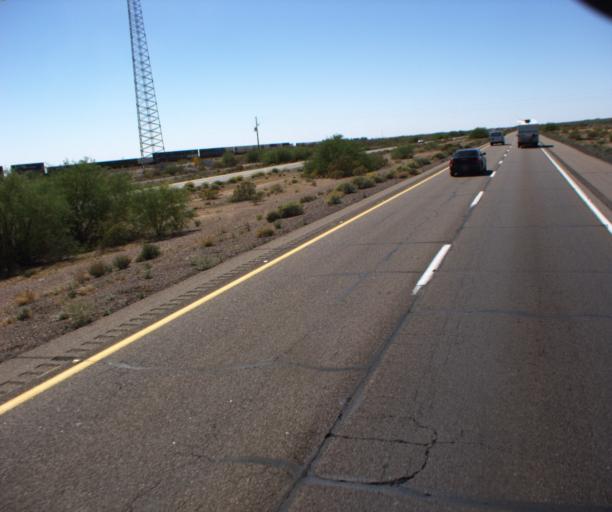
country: US
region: Arizona
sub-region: Maricopa County
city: Gila Bend
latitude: 32.9071
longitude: -112.9825
